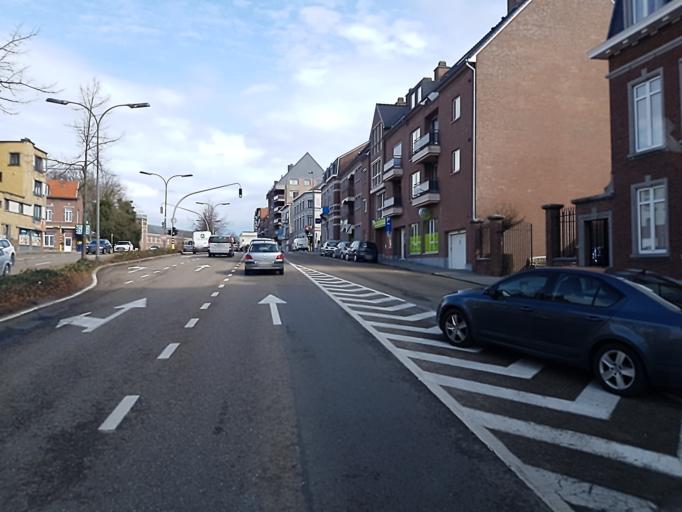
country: BE
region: Flanders
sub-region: Provincie Limburg
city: Tongeren
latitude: 50.7792
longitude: 5.4603
